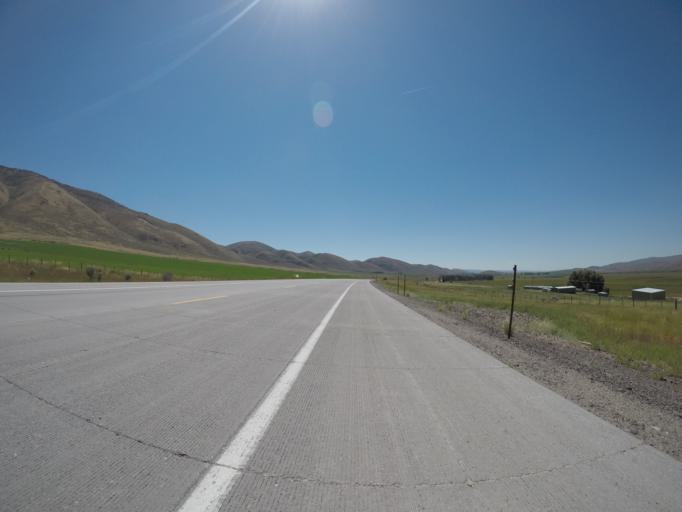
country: US
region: Idaho
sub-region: Bear Lake County
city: Montpelier
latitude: 42.1738
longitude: -110.9958
